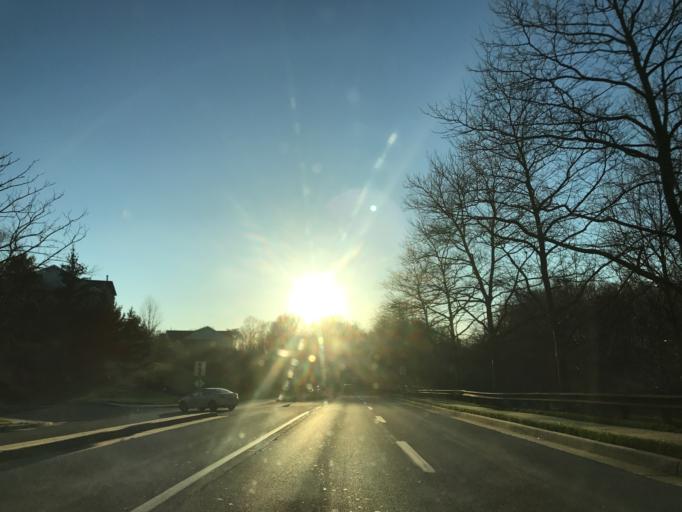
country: US
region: Maryland
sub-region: Baltimore County
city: Owings Mills
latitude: 39.4025
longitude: -76.8046
